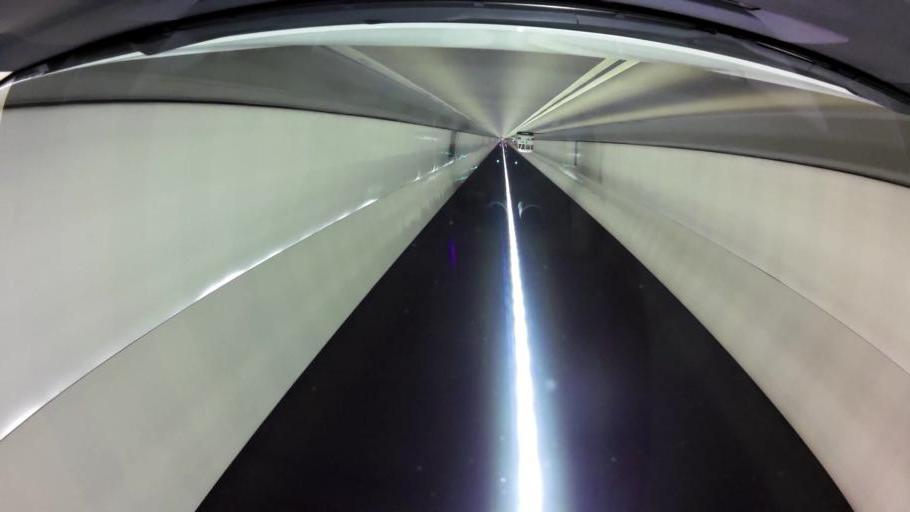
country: HK
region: Sha Tin
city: Sha Tin
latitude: 22.3782
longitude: 114.1577
